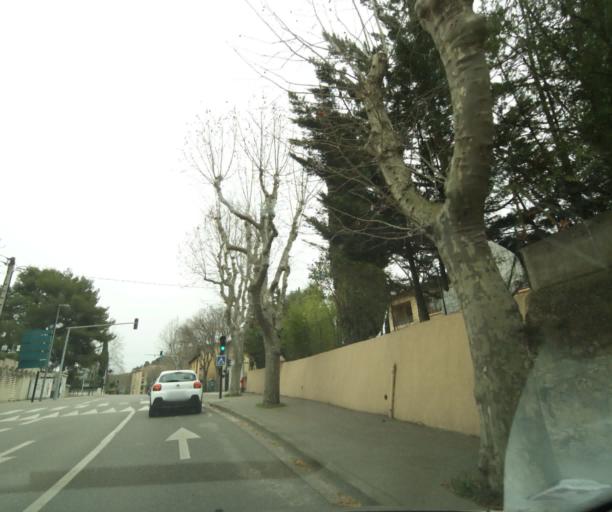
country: FR
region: Provence-Alpes-Cote d'Azur
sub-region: Departement des Bouches-du-Rhone
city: Aix-en-Provence
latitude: 43.5338
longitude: 5.4619
